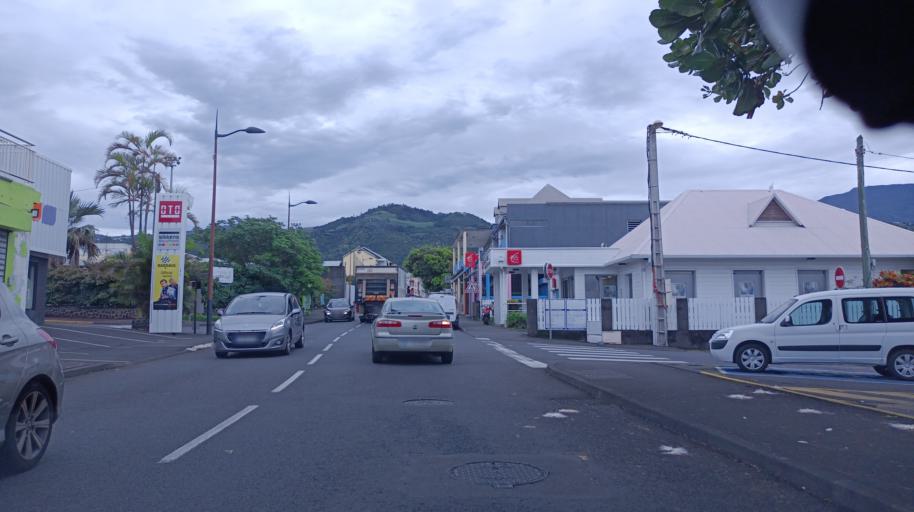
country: RE
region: Reunion
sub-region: Reunion
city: Saint-Joseph
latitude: -21.3796
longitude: 55.6155
